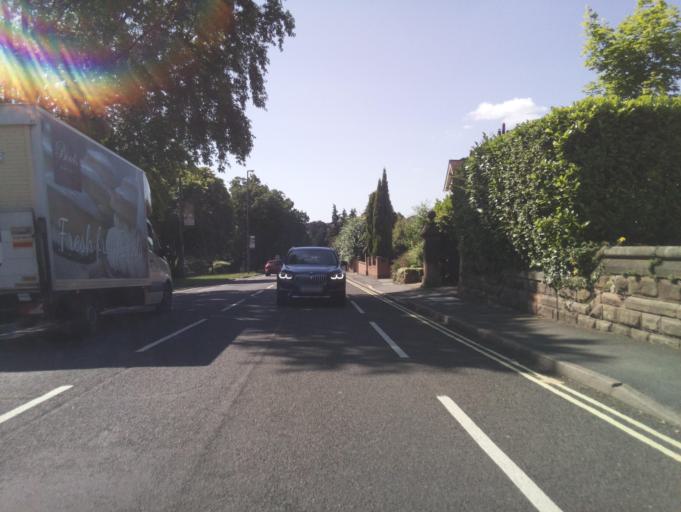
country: GB
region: England
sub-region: Derby
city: Derby
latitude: 52.9399
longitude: -1.4842
